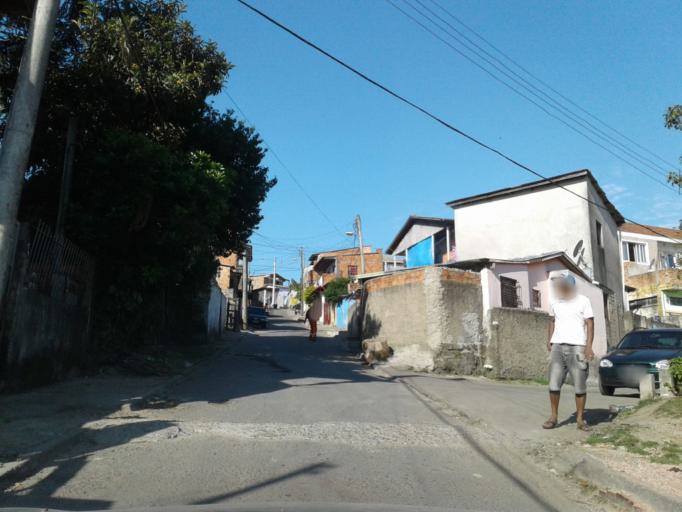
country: BR
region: Rio Grande do Sul
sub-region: Porto Alegre
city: Porto Alegre
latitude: -30.0457
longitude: -51.1522
